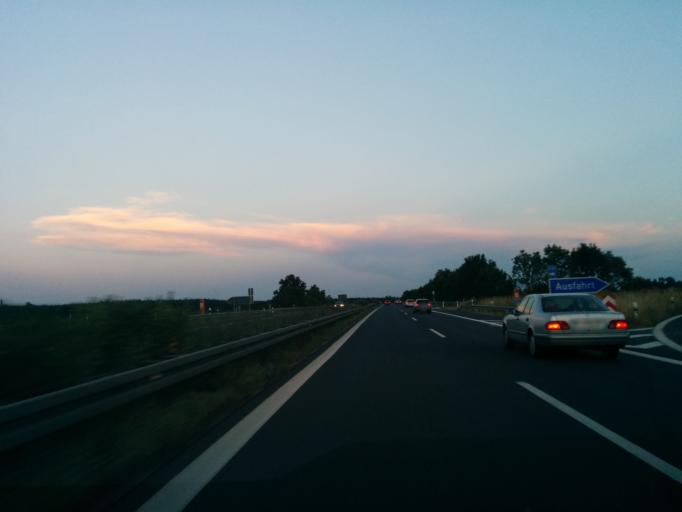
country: DE
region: Bavaria
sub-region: Upper Franconia
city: Kemmern
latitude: 49.9612
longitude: 10.8831
